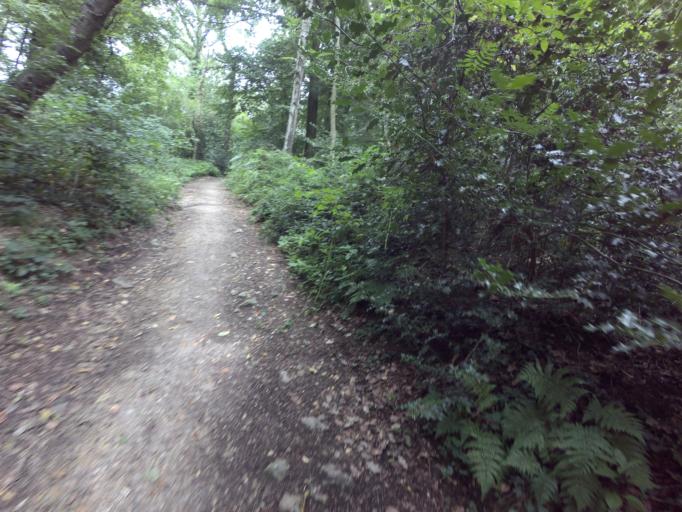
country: NL
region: Limburg
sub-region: Valkenburg aan de Geul
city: Schin op Geul
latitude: 50.7830
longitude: 5.8888
